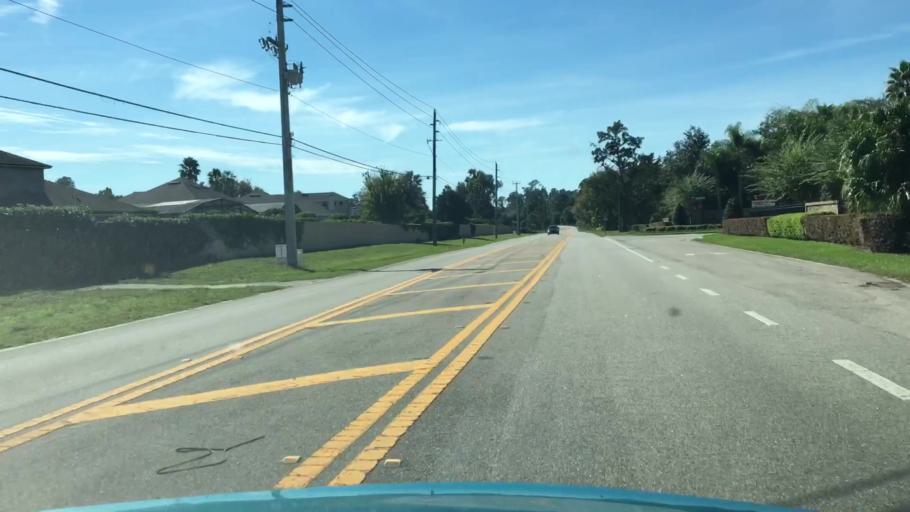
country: US
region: Florida
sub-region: Seminole County
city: Heathrow
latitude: 28.8227
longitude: -81.3589
